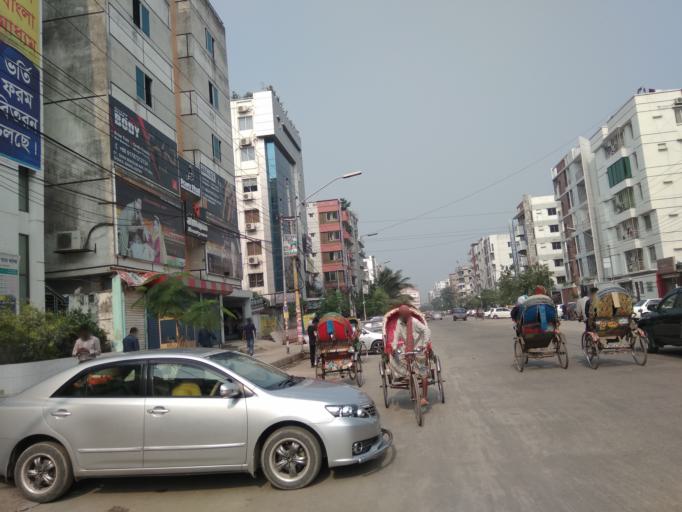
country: BD
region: Dhaka
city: Tungi
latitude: 23.8705
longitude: 90.3839
